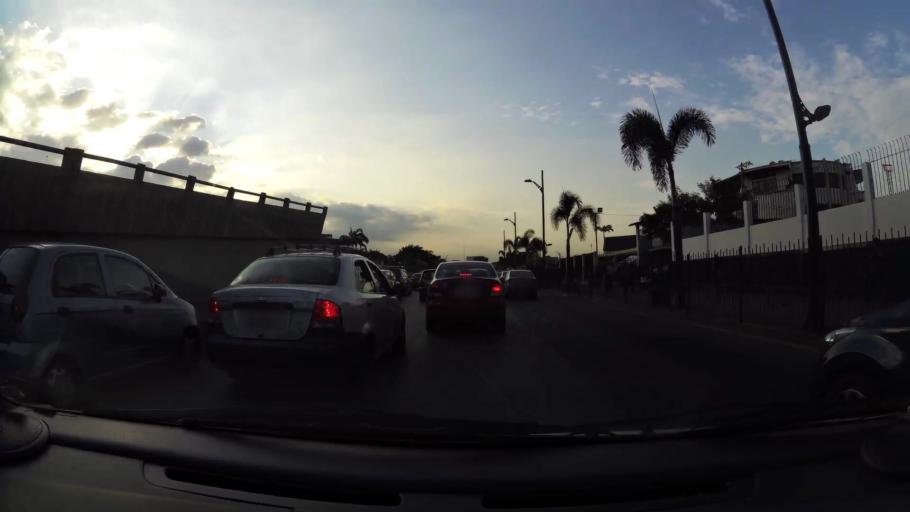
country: EC
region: Guayas
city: Guayaquil
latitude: -2.1766
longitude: -79.8914
